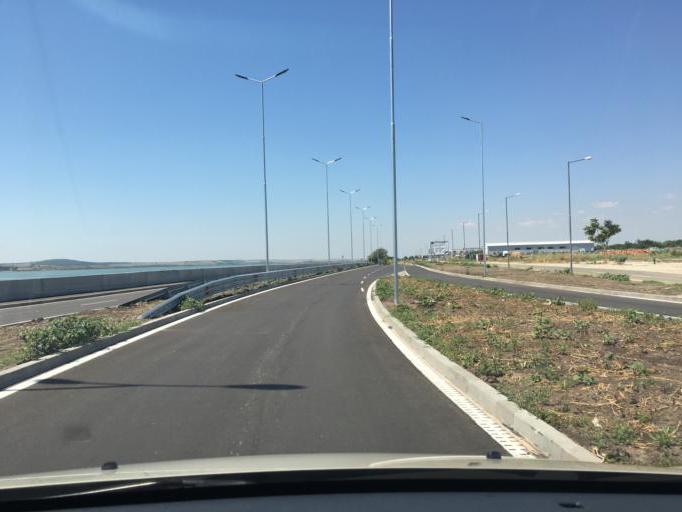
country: BG
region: Burgas
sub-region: Obshtina Burgas
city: Burgas
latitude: 42.5117
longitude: 27.4333
